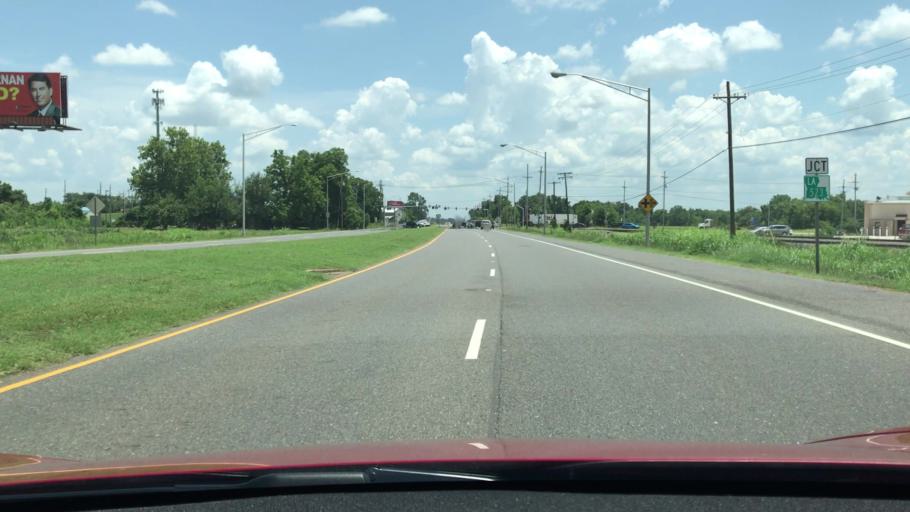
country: US
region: Louisiana
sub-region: Bossier Parish
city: Bossier City
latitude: 32.4027
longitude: -93.6951
